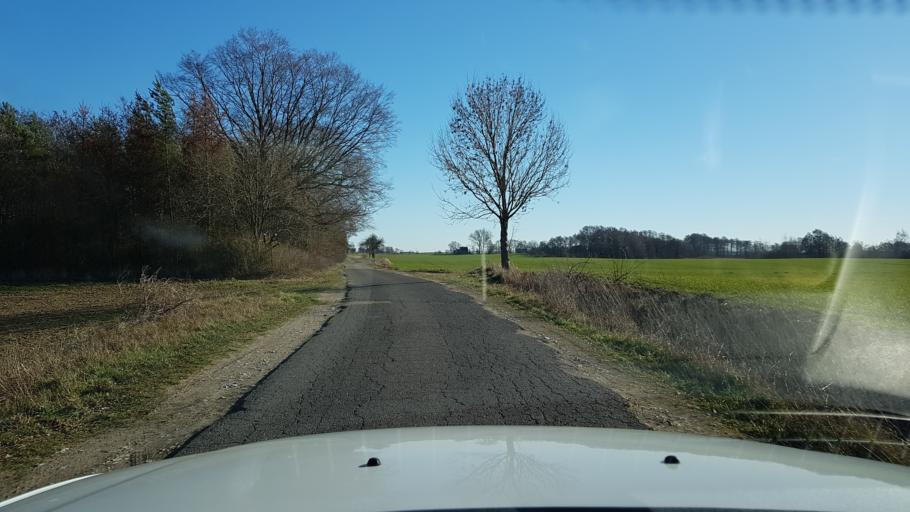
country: PL
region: West Pomeranian Voivodeship
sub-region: Powiat mysliborski
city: Barlinek
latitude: 53.0082
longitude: 15.1476
